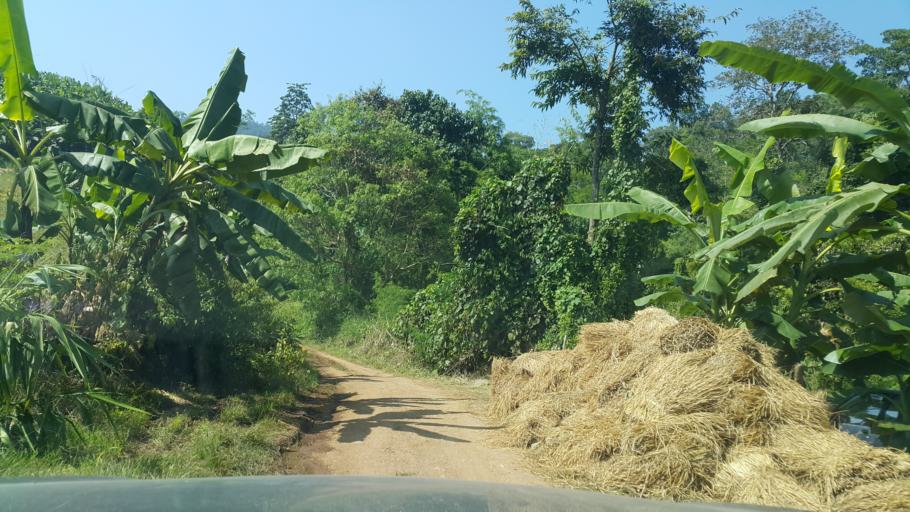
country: TH
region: Chiang Mai
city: Samoeng
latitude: 18.9389
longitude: 98.6175
